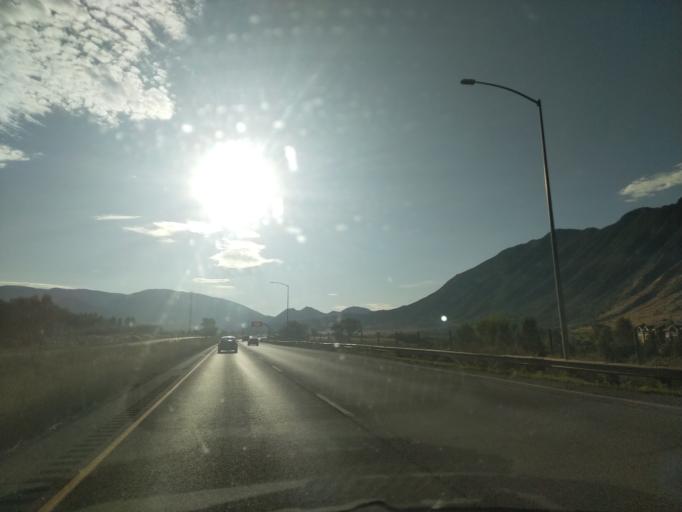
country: US
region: Colorado
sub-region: Garfield County
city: New Castle
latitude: 39.5657
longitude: -107.5126
